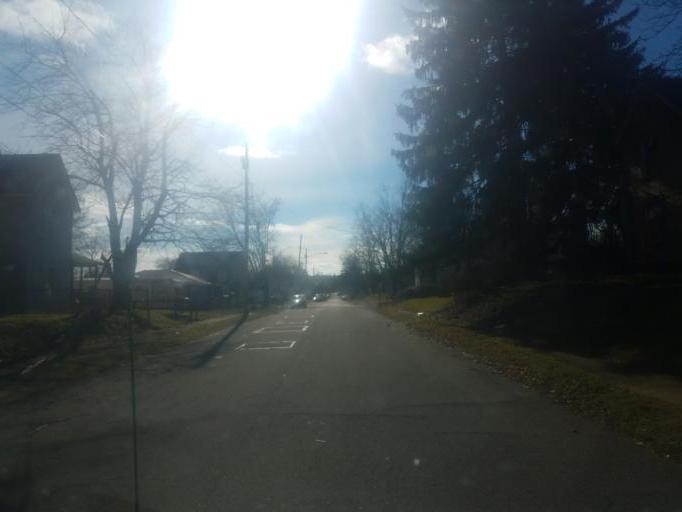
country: US
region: Ohio
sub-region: Richland County
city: Mansfield
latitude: 40.7743
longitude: -82.5178
